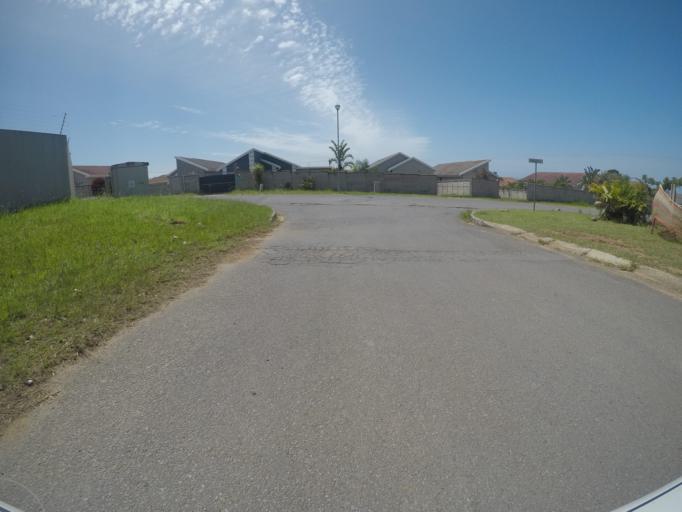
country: ZA
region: Eastern Cape
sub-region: Buffalo City Metropolitan Municipality
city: East London
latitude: -32.9429
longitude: 27.9944
